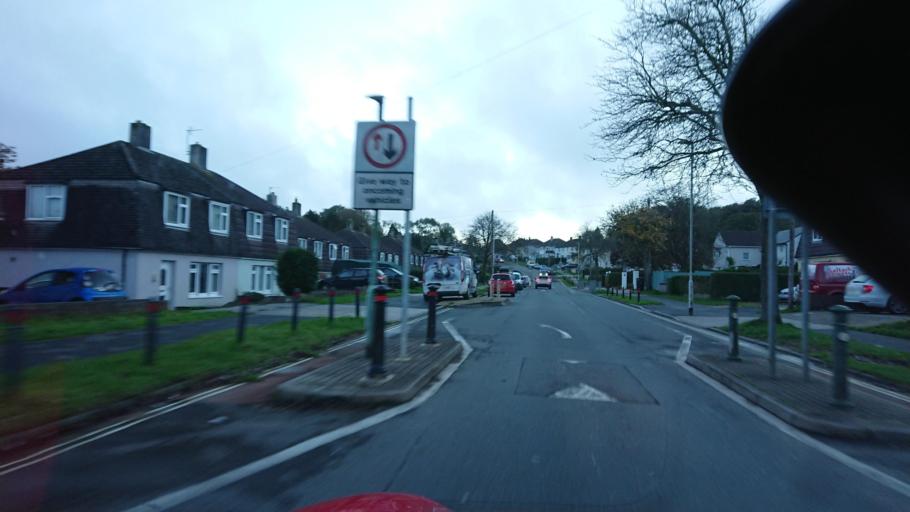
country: GB
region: England
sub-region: Cornwall
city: Torpoint
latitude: 50.4172
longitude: -4.1712
